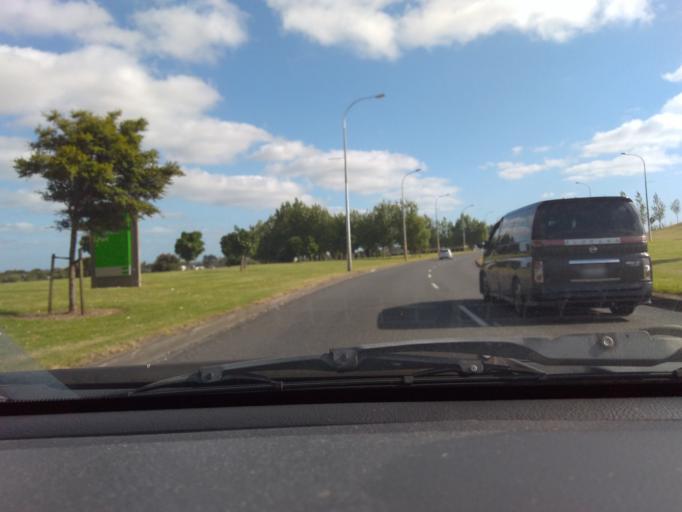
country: NZ
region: Auckland
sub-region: Auckland
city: Manukau City
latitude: -36.9425
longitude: 174.8626
